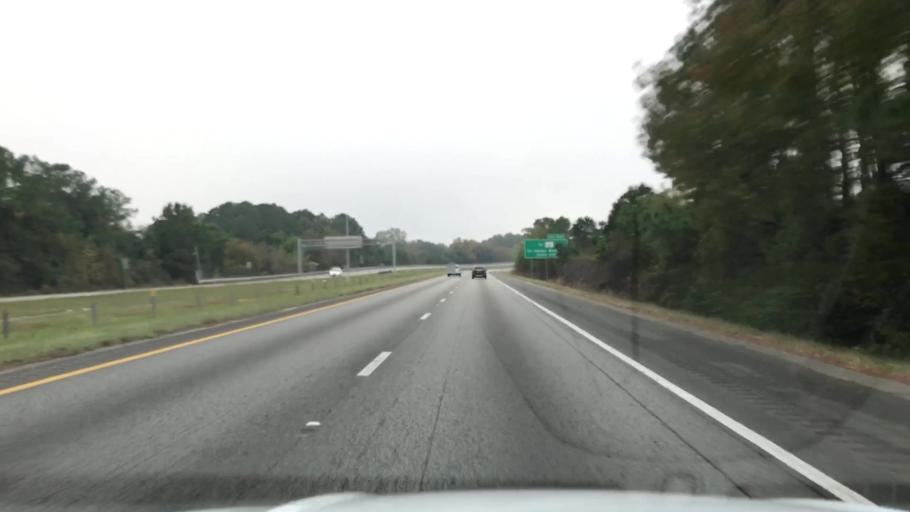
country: US
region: South Carolina
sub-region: Charleston County
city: North Charleston
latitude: 32.8218
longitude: -80.0307
